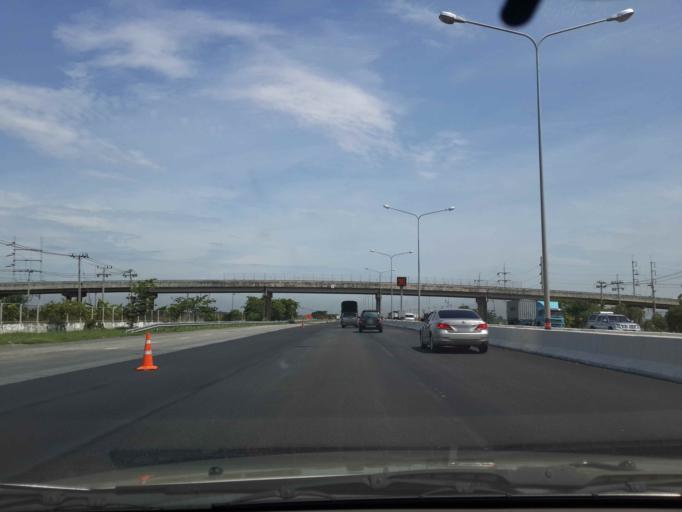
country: TH
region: Samut Prakan
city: Ban Khlong Bang Sao Thong
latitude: 13.6488
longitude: 100.8766
